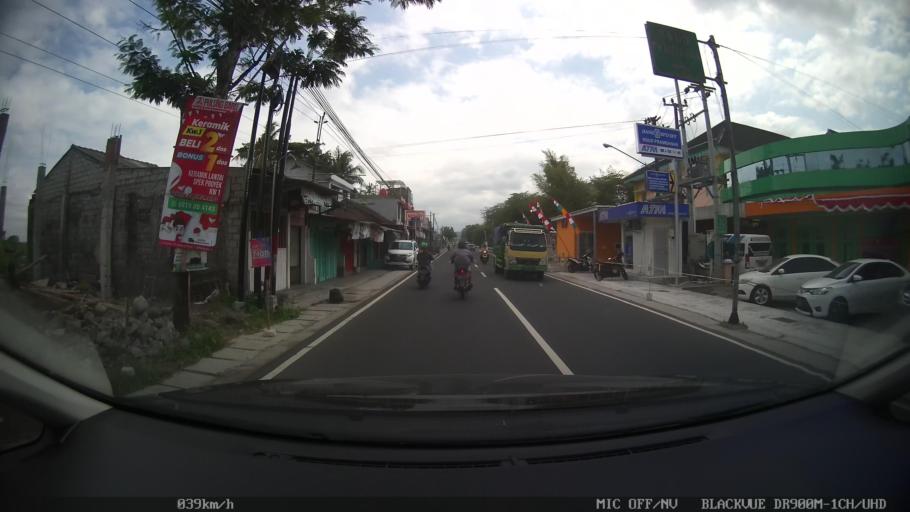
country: ID
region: Central Java
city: Candi Prambanan
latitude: -7.8045
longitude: 110.4829
